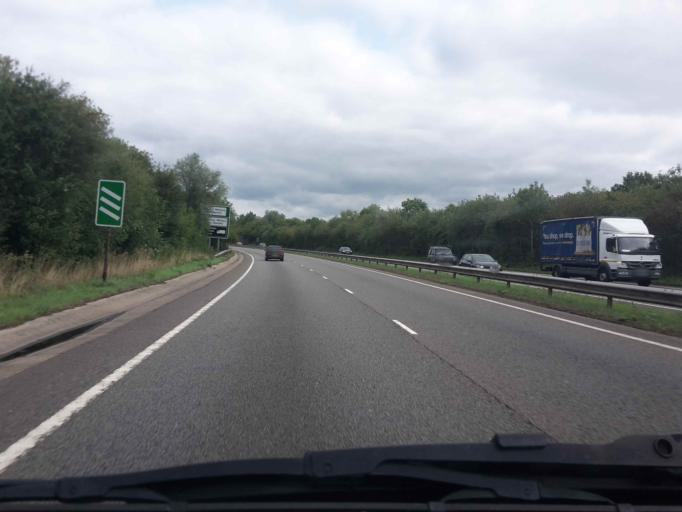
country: GB
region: England
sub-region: Surrey
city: Seale
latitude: 51.2345
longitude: -0.7357
